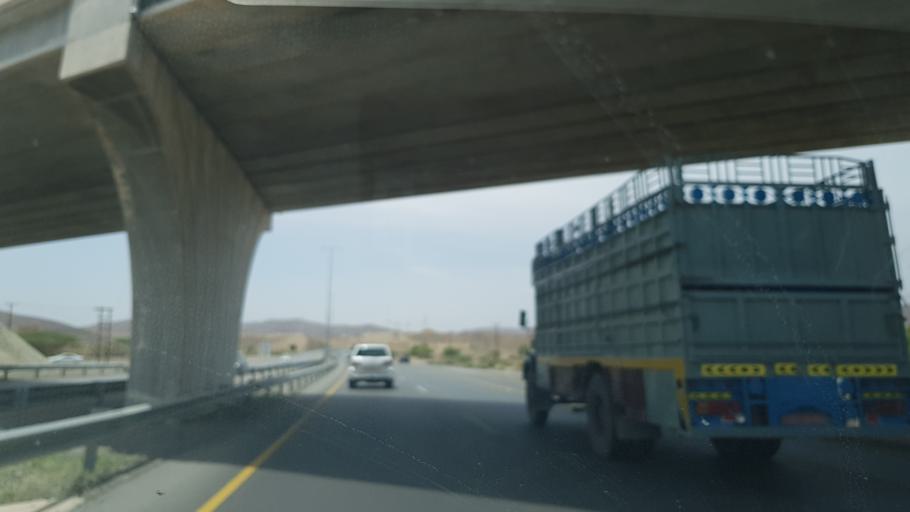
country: OM
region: Muhafazat ad Dakhiliyah
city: Izki
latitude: 22.9140
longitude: 57.7675
